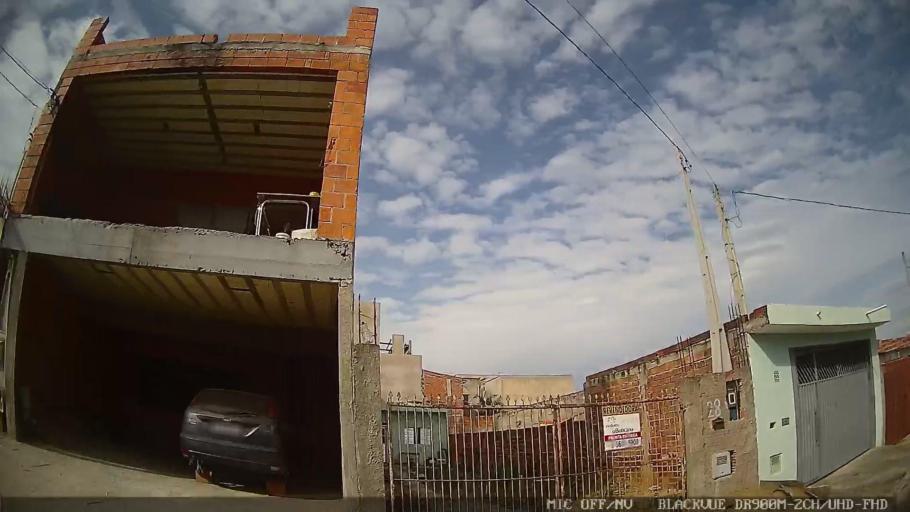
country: BR
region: Sao Paulo
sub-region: Salto
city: Salto
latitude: -23.1846
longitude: -47.2611
